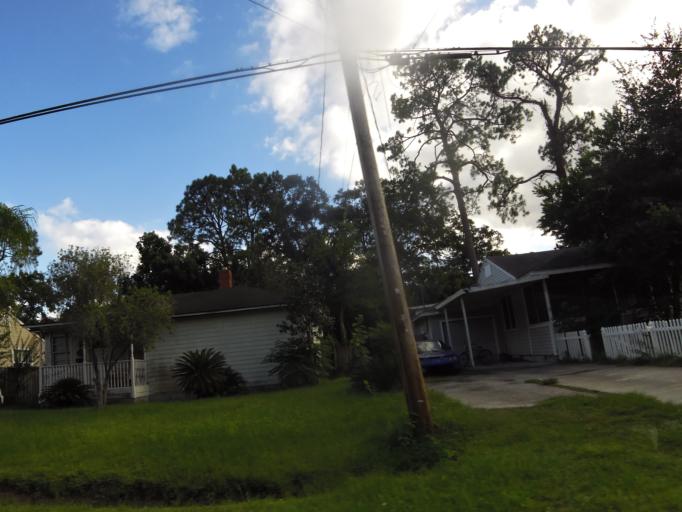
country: US
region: Florida
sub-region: Duval County
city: Jacksonville
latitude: 30.2869
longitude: -81.7291
